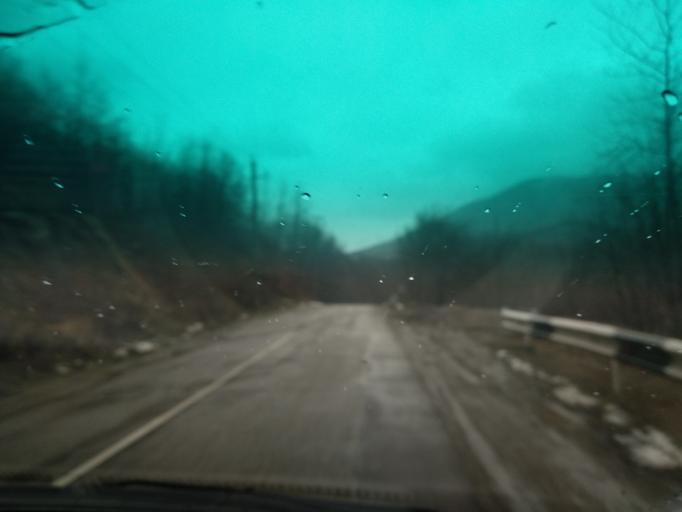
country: RU
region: Krasnodarskiy
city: Khadyzhensk
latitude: 44.2238
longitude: 39.3896
